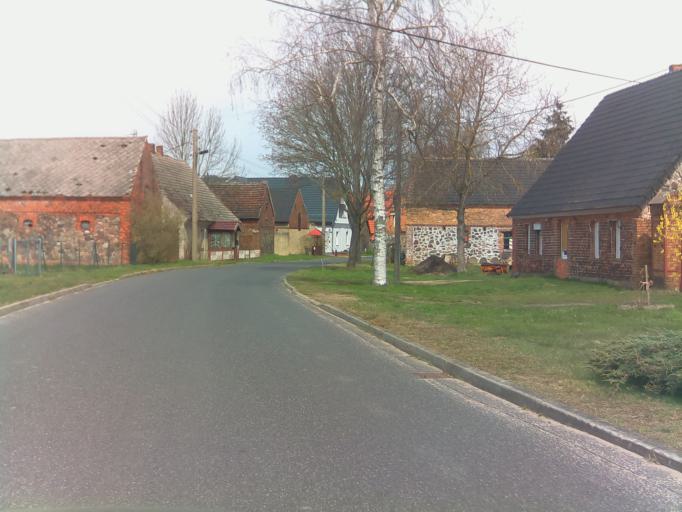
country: DE
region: Brandenburg
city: Bronkow
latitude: 51.7005
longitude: 13.8745
